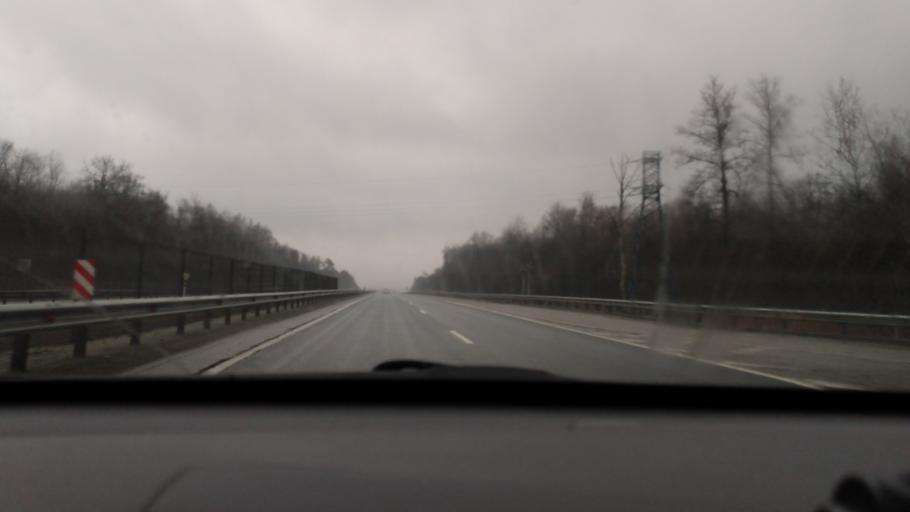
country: RU
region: Moskovskaya
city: Stupino
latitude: 54.8672
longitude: 38.0305
